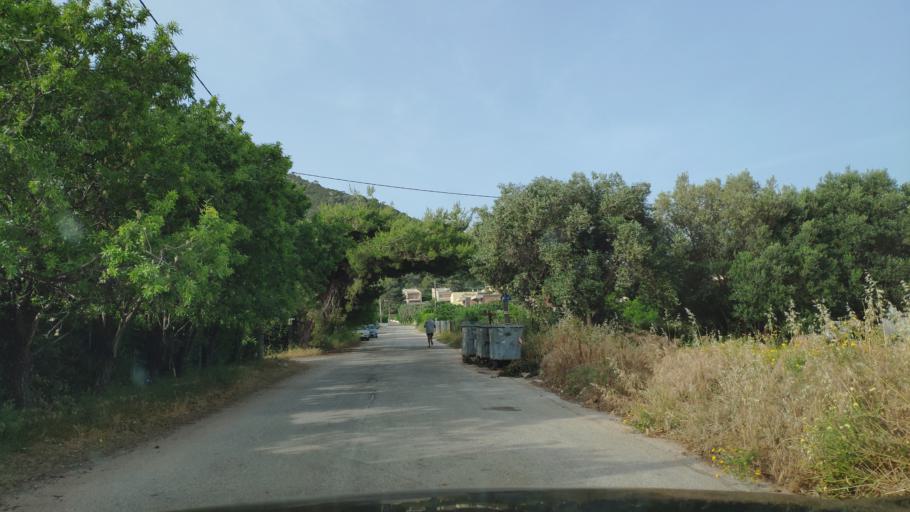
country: GR
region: Attica
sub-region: Nomarchia Anatolikis Attikis
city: Limin Mesoyaias
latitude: 37.8635
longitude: 24.0296
